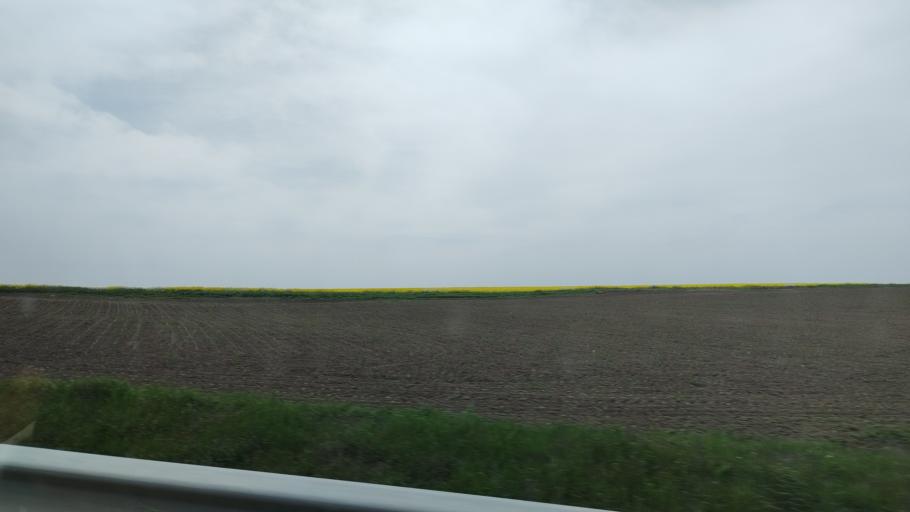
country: RO
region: Constanta
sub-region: Comuna Deleni
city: Pietreni
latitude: 44.0826
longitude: 28.1267
